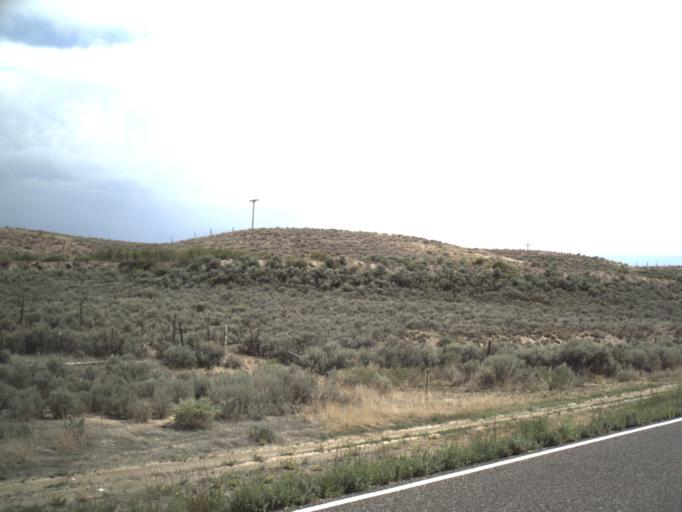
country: US
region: Utah
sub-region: Piute County
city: Junction
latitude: 38.1300
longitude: -112.0002
